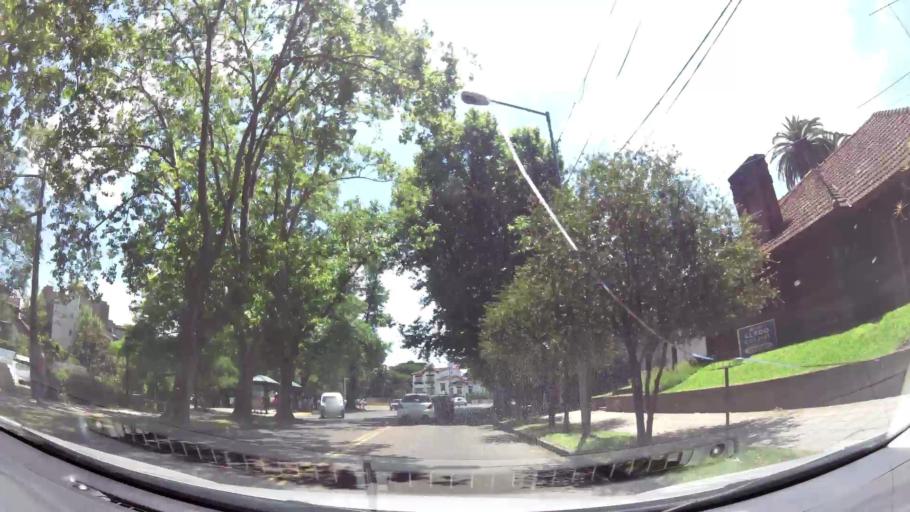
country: AR
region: Buenos Aires
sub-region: Partido de Tigre
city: Tigre
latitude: -34.4196
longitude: -58.5878
